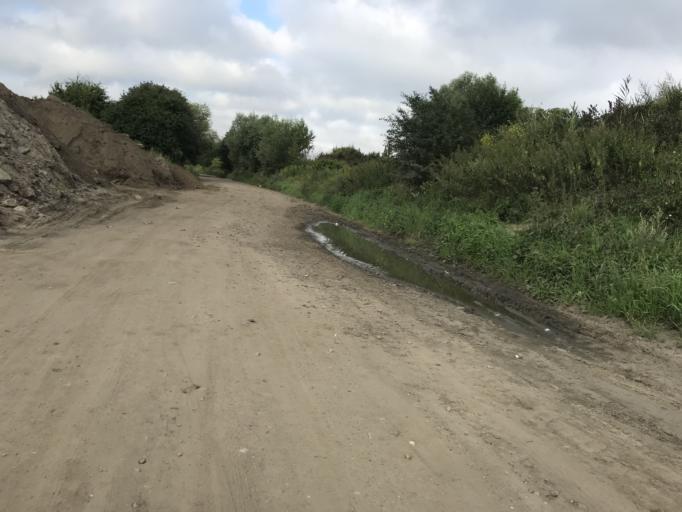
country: PL
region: Pomeranian Voivodeship
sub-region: Gdansk
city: Gdansk
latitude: 54.3405
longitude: 18.6851
